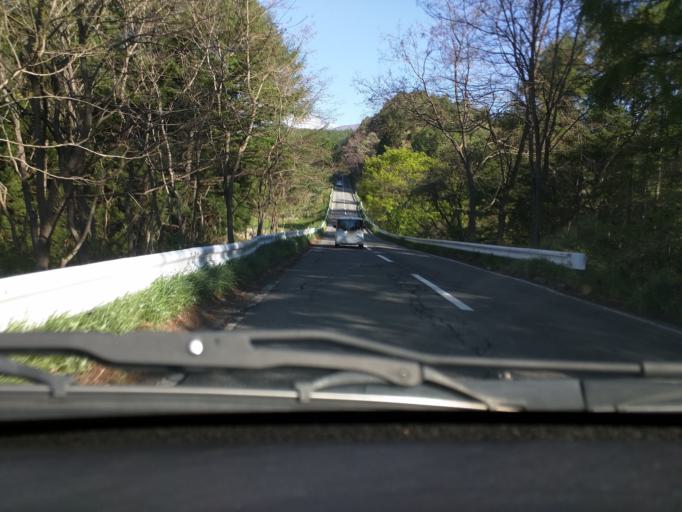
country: JP
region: Nagano
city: Nagano-shi
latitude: 36.6877
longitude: 138.1584
